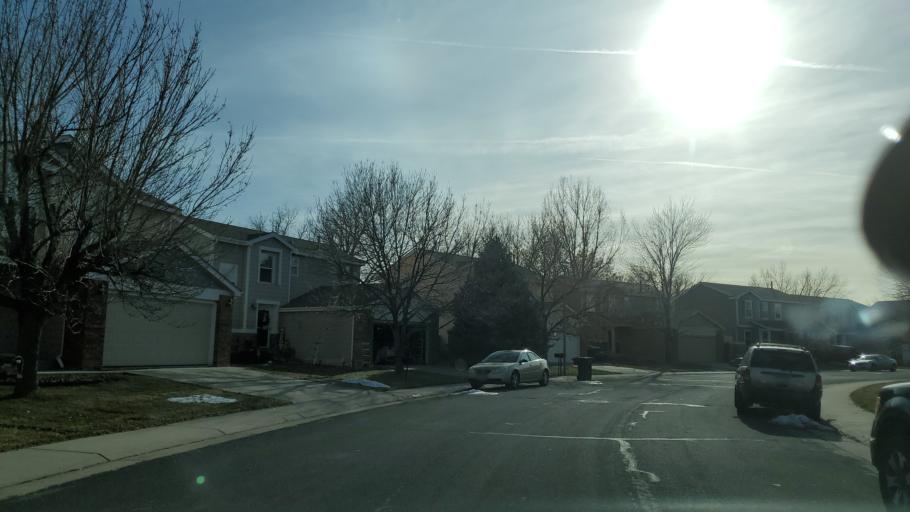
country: US
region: Colorado
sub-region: Adams County
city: Northglenn
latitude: 39.9106
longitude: -104.9519
